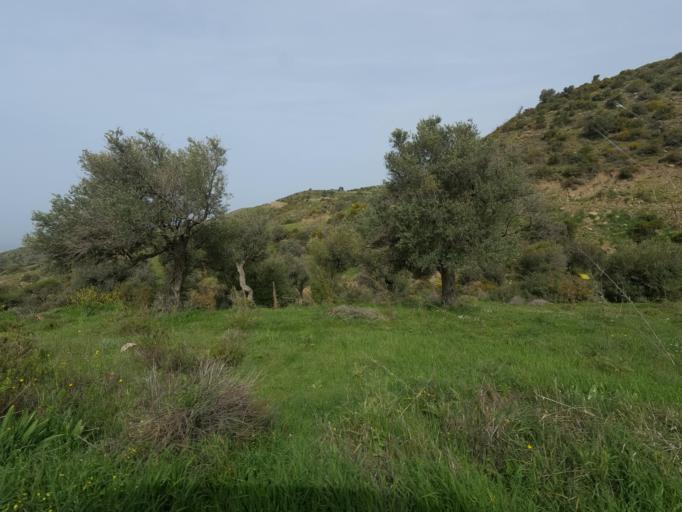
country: CY
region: Pafos
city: Pegeia
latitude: 34.9483
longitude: 32.3564
